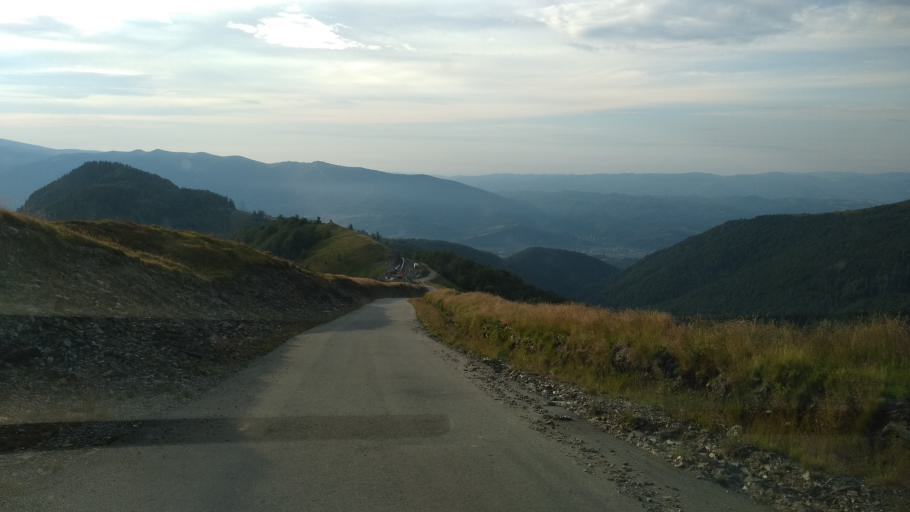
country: RO
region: Hunedoara
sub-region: Municipiul  Vulcan
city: Jiu-Paroseni
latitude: 45.3138
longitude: 23.3060
